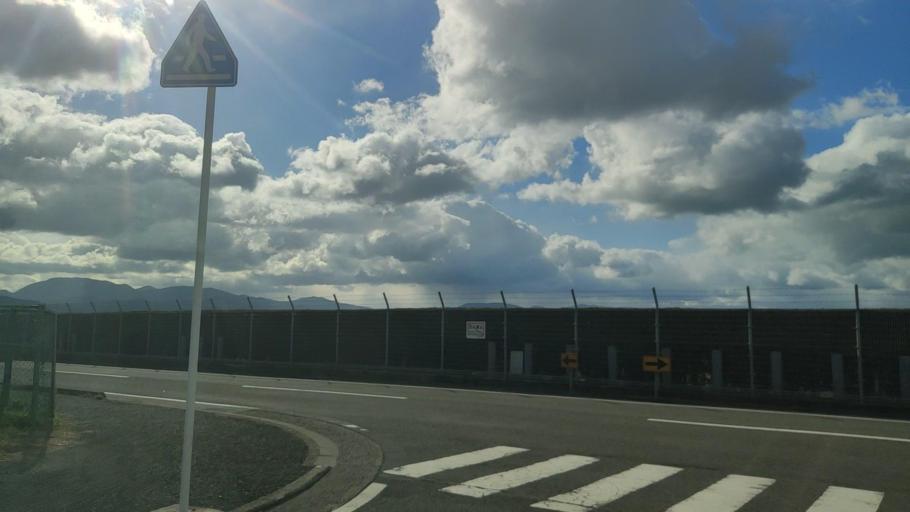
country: JP
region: Ehime
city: Masaki-cho
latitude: 33.8240
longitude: 132.7084
